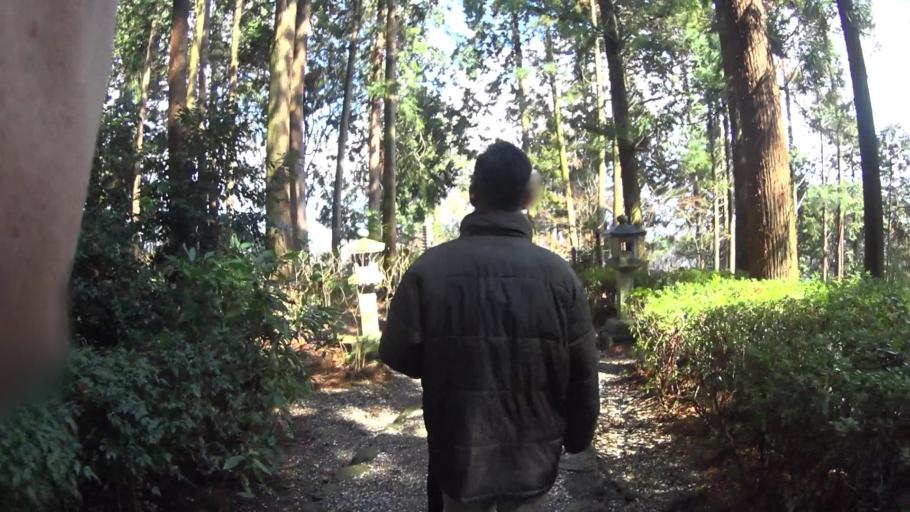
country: JP
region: Kyoto
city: Muko
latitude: 34.9388
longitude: 135.6429
